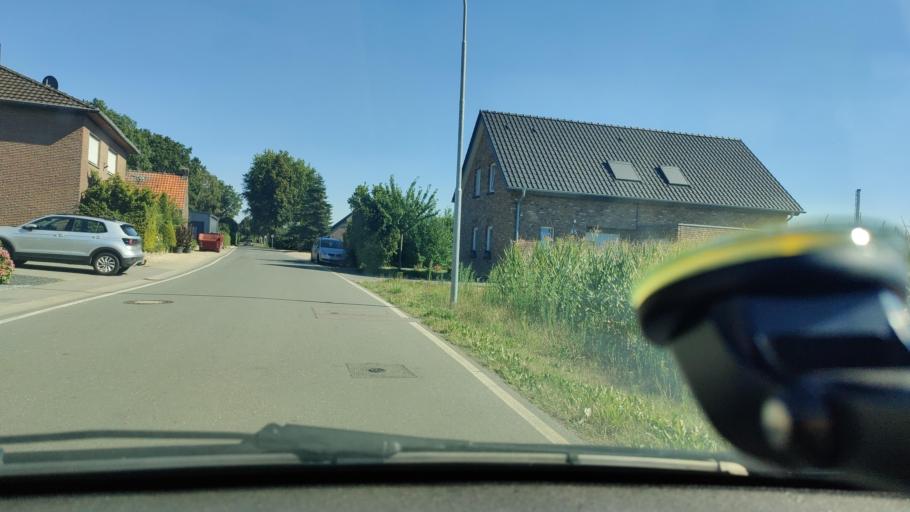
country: DE
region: North Rhine-Westphalia
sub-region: Regierungsbezirk Dusseldorf
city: Wachtendonk
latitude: 51.4631
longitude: 6.3586
